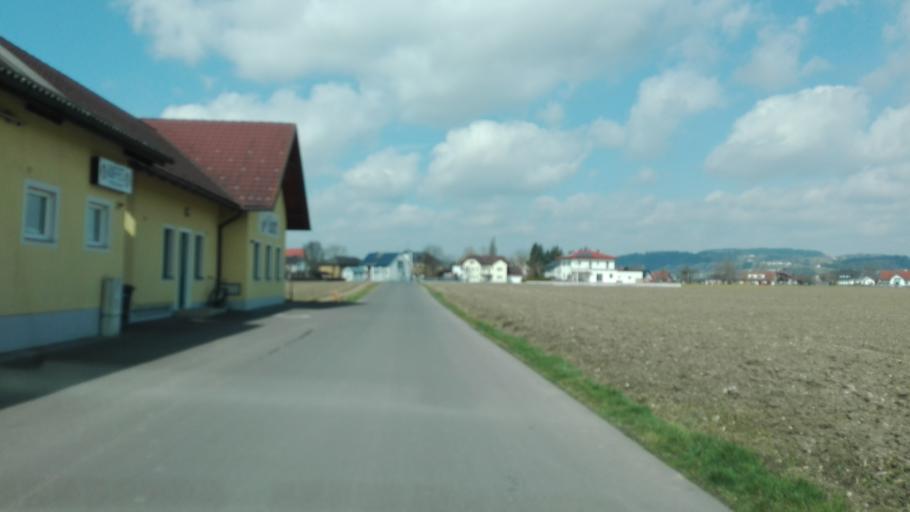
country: AT
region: Upper Austria
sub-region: Politischer Bezirk Urfahr-Umgebung
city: Goldworth
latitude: 48.3245
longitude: 14.1043
